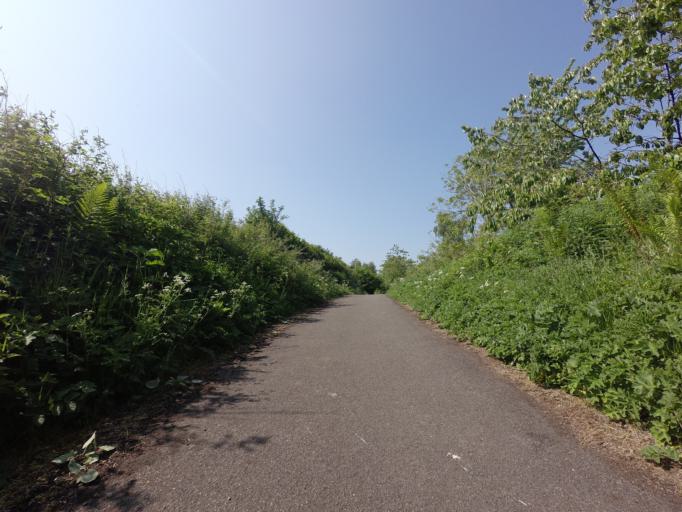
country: GB
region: Scotland
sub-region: Fife
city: Townhill
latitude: 56.0936
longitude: -3.4421
